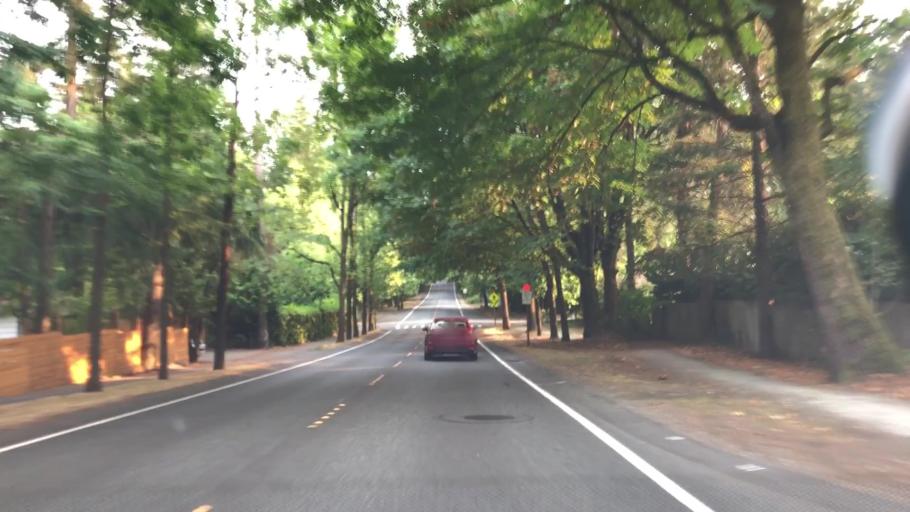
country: US
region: Washington
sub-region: King County
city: Mercer Island
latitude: 47.5469
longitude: -122.2216
